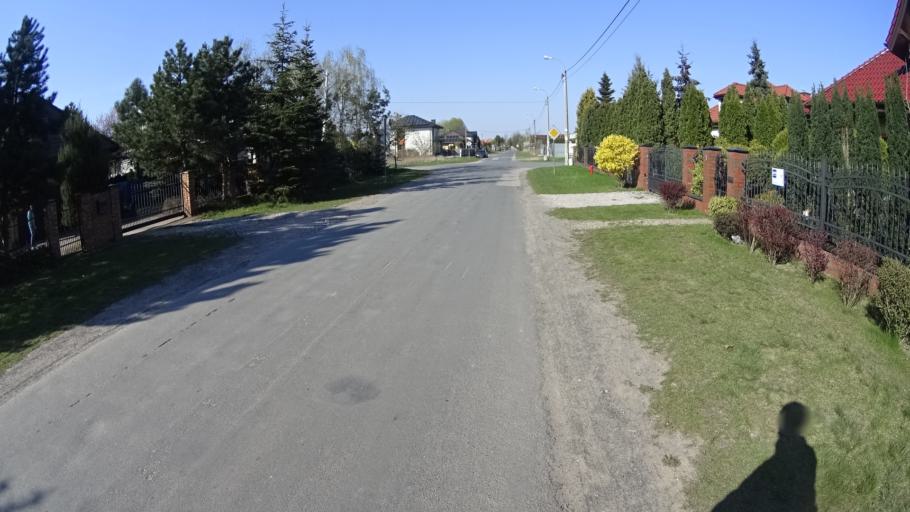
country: PL
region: Masovian Voivodeship
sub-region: Powiat warszawski zachodni
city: Babice
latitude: 52.2569
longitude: 20.8439
